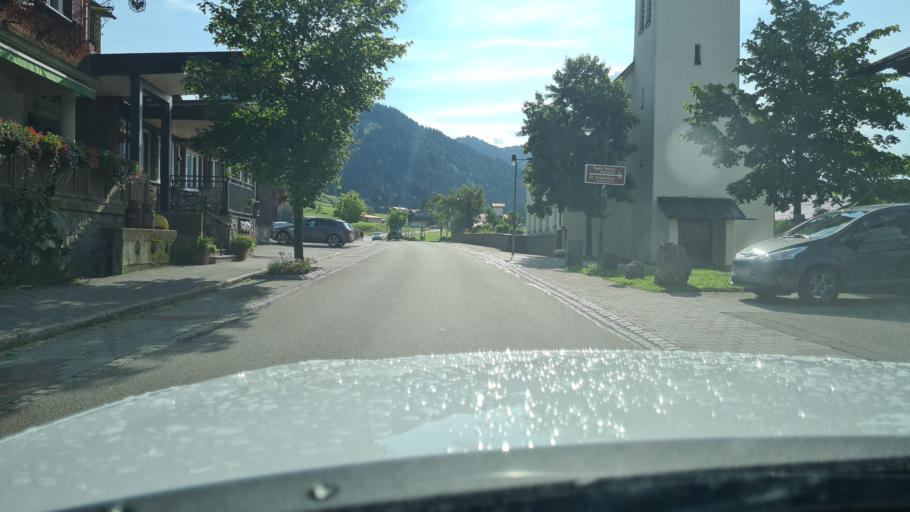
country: DE
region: Bavaria
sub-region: Swabia
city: Balderschwang
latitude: 47.4658
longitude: 10.1036
